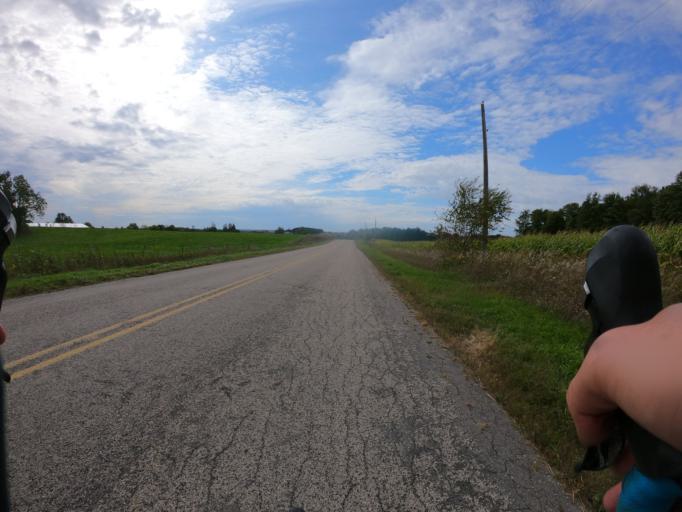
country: CA
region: Ontario
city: Kitchener
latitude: 43.3759
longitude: -80.6108
